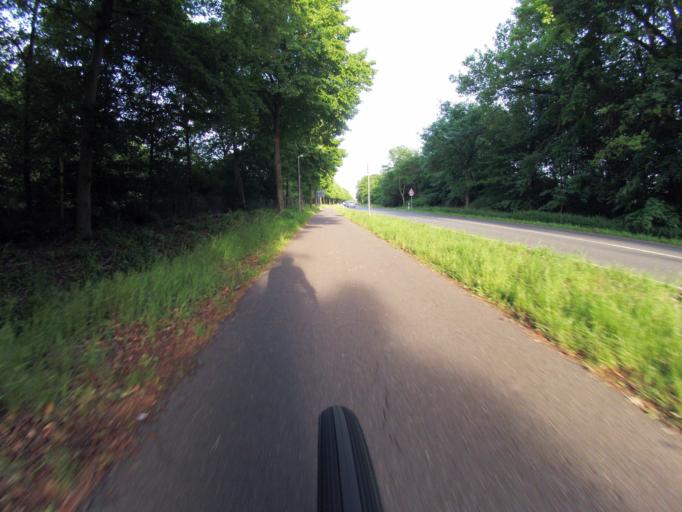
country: DE
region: North Rhine-Westphalia
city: Ibbenburen
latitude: 52.2649
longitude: 7.7446
